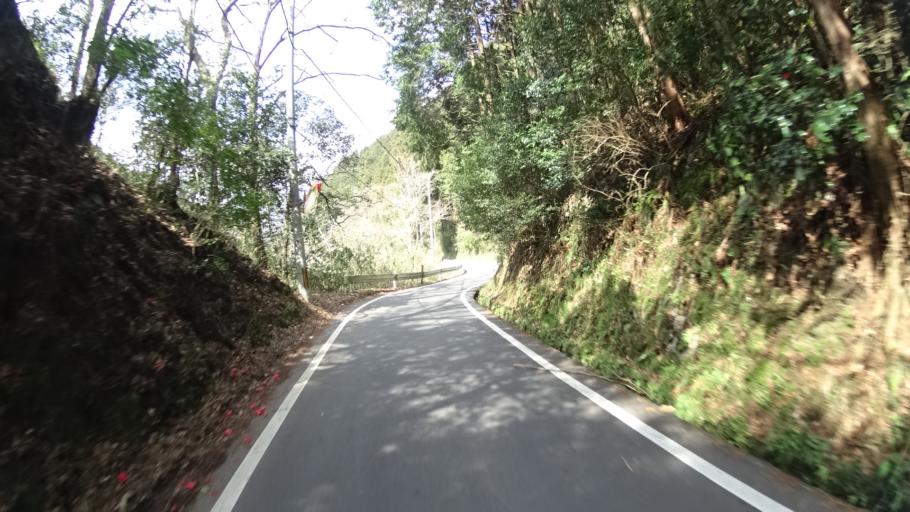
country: JP
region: Nara
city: Nara-shi
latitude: 34.7462
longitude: 135.9408
